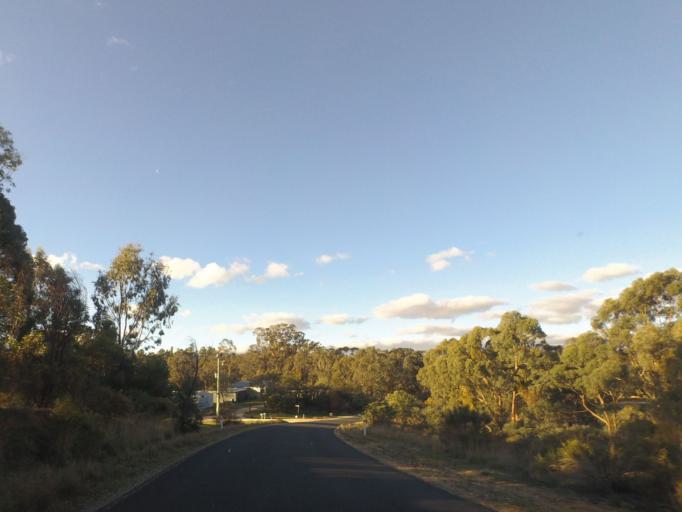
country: AU
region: Victoria
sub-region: Mount Alexander
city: Castlemaine
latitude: -37.1568
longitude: 144.2215
